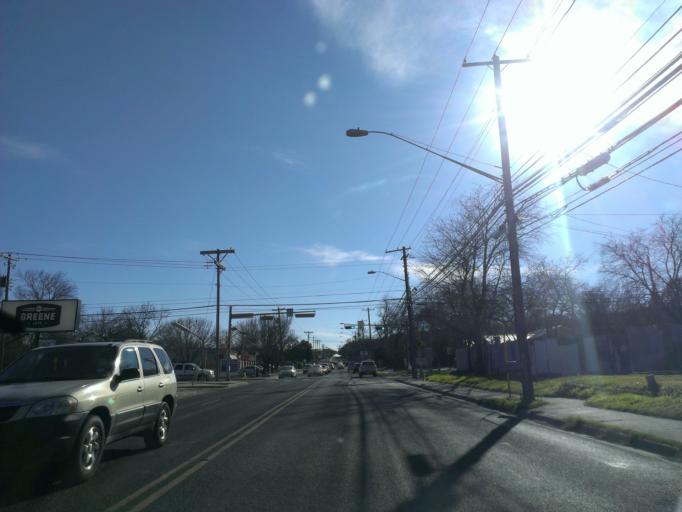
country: US
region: Texas
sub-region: Travis County
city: Austin
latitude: 30.2388
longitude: -97.7618
